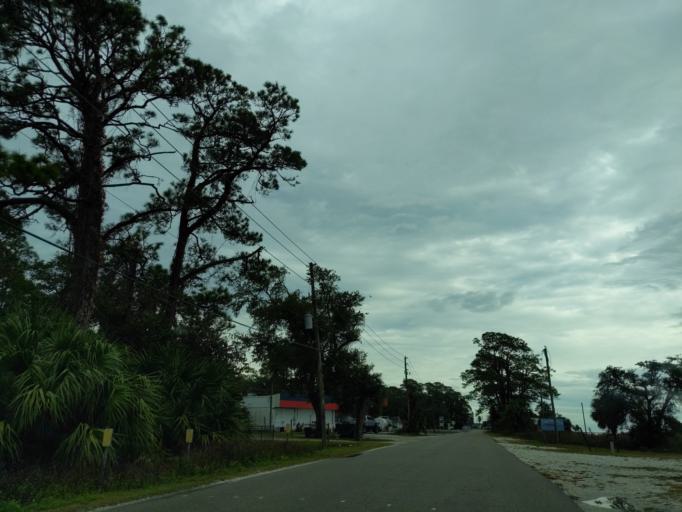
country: US
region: Florida
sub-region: Franklin County
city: Eastpoint
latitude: 29.7357
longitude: -84.8802
